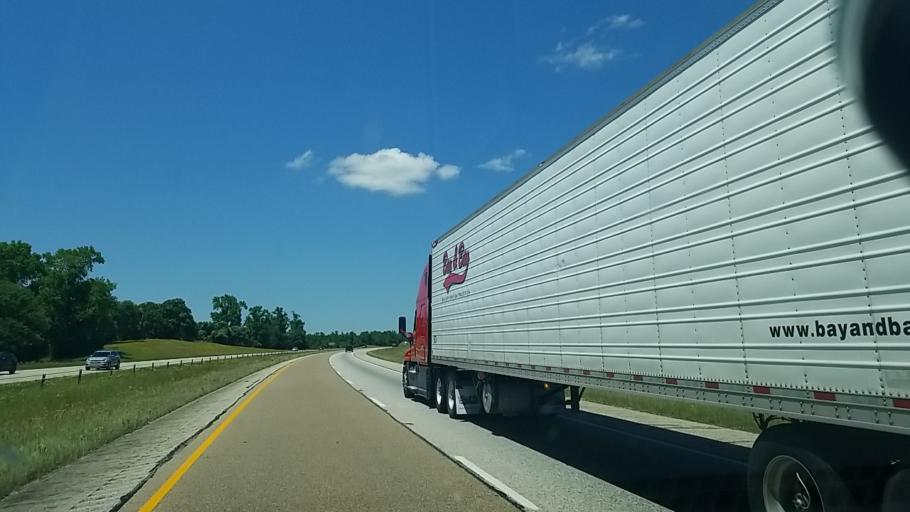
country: US
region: Texas
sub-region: Leon County
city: Centerville
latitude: 31.2094
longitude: -95.9966
